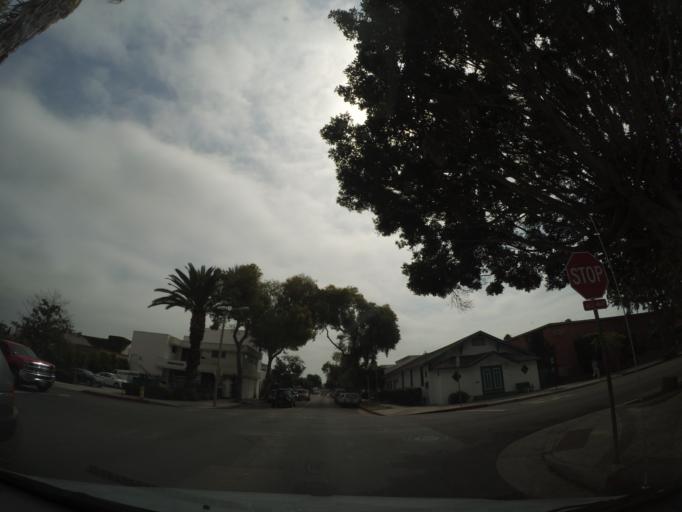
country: US
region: California
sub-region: Santa Barbara County
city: Santa Barbara
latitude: 34.4211
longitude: -119.6937
